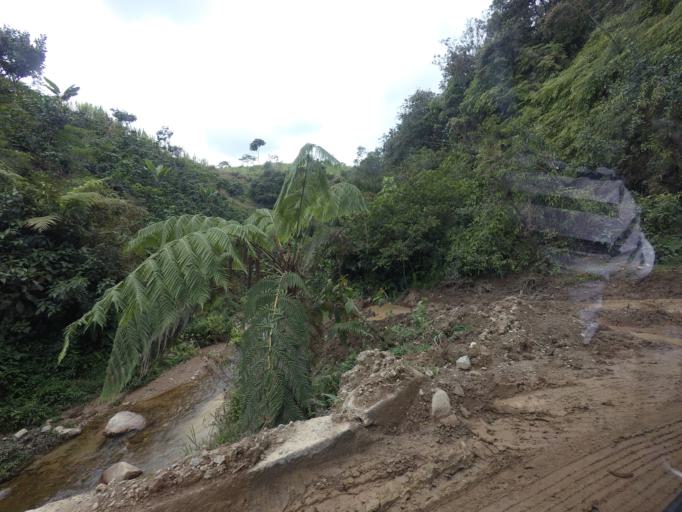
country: CO
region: Huila
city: San Agustin
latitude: 1.9575
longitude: -76.2975
